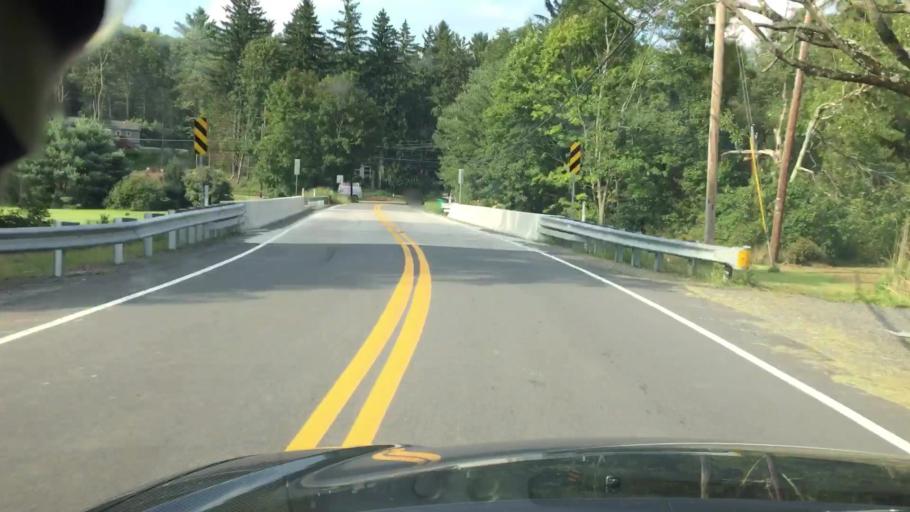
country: US
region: Pennsylvania
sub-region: Luzerne County
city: Harleigh
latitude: 41.0291
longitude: -75.9898
